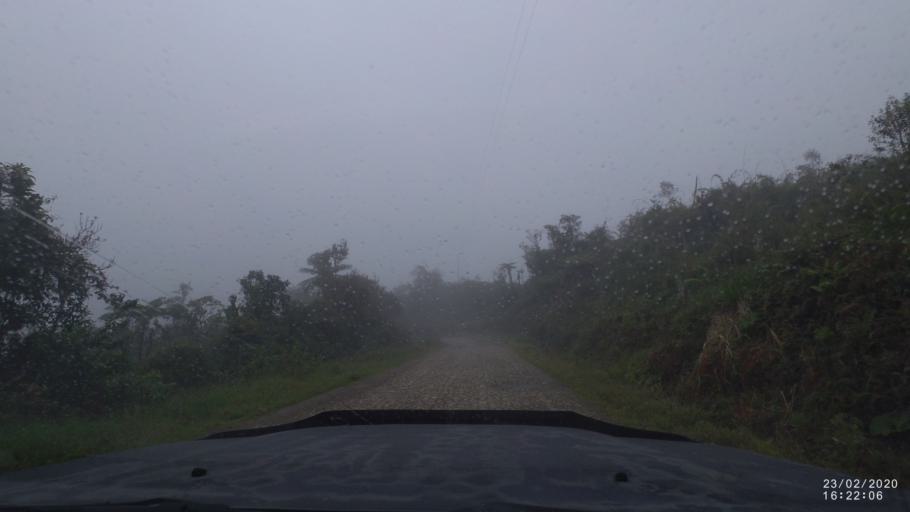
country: BO
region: Cochabamba
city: Colomi
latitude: -17.1118
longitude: -65.9701
